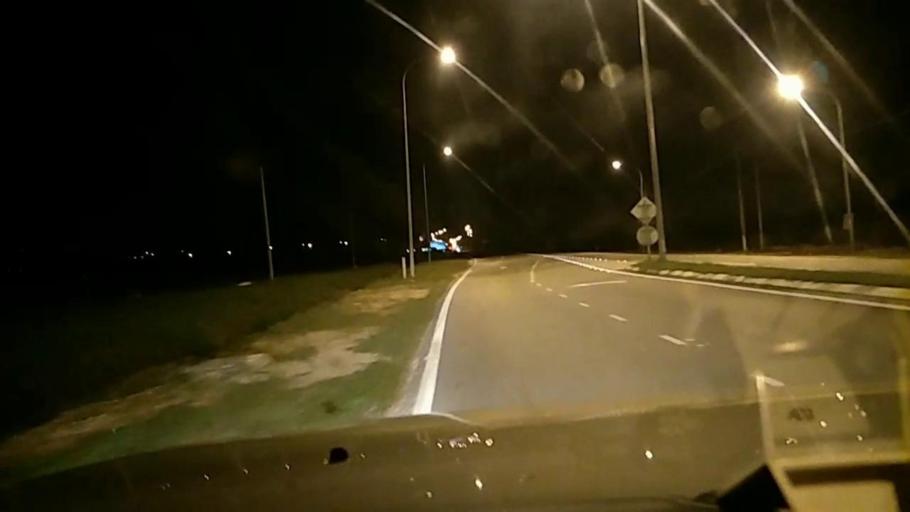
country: MY
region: Selangor
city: Ladang Seri Kundang
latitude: 3.2340
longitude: 101.4557
